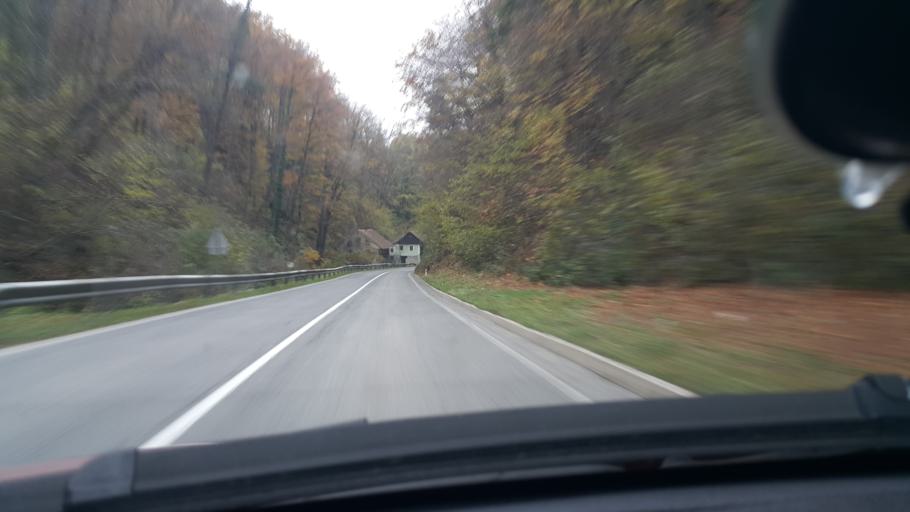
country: SI
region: Bistrica ob Sotli
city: Bistrica ob Sotli
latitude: 46.0505
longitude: 15.6655
